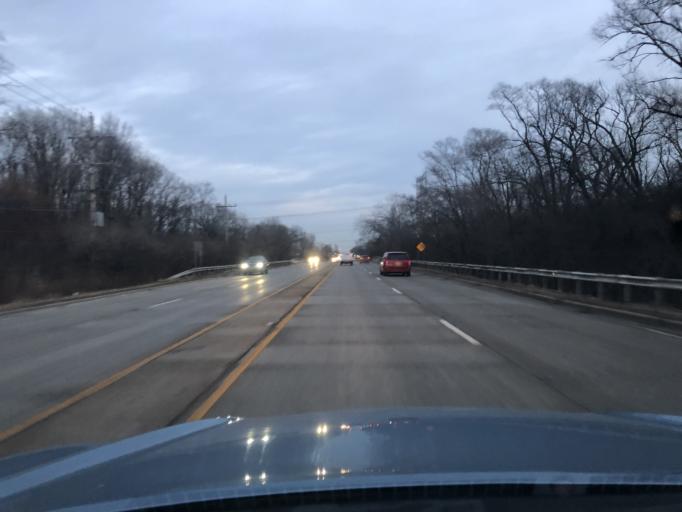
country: US
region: Illinois
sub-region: DuPage County
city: Itasca
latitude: 41.9927
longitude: -87.9974
